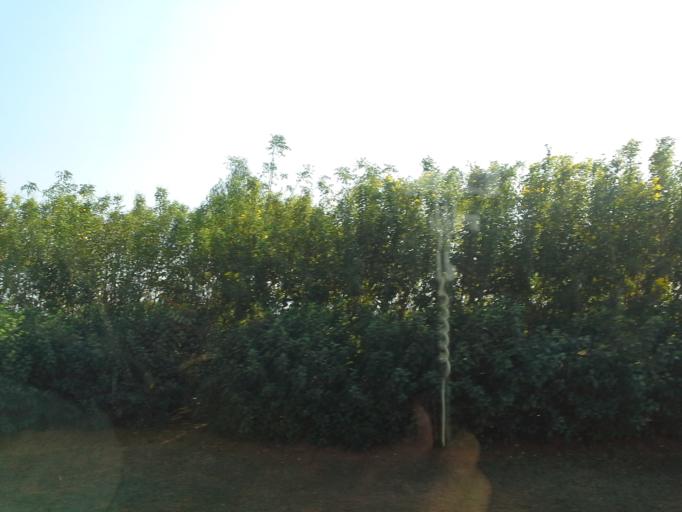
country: IN
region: Telangana
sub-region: Rangareddi
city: Balapur
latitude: 17.2450
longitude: 78.3988
